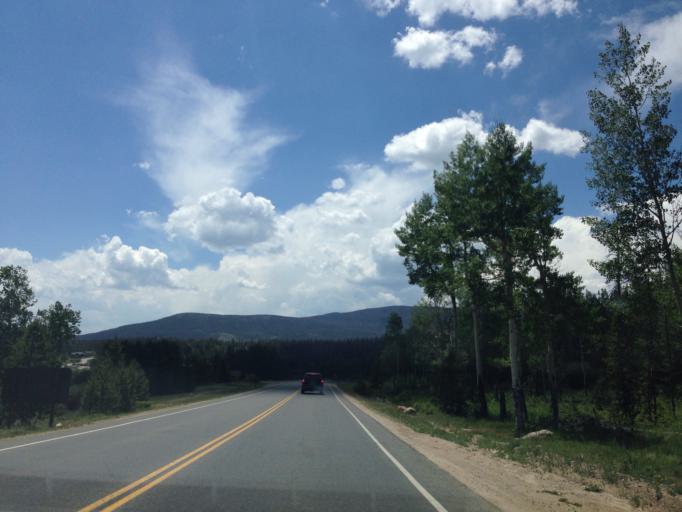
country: US
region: Colorado
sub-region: Grand County
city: Granby
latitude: 40.2595
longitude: -105.8334
